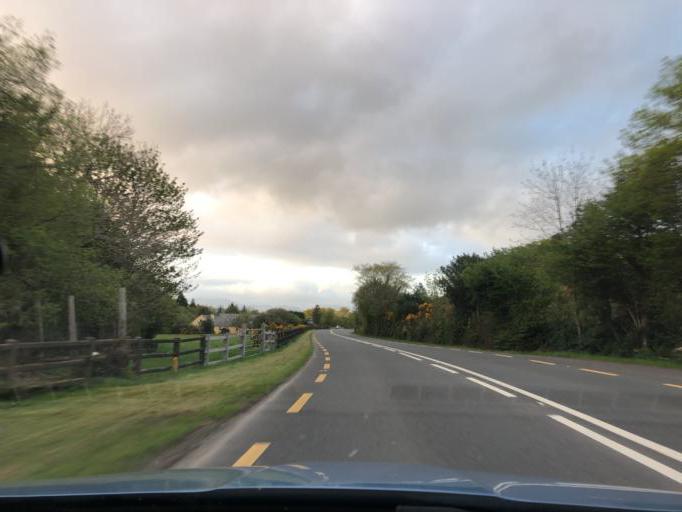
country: IE
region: Munster
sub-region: Ciarrai
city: Killorglin
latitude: 52.0491
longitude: -9.9472
